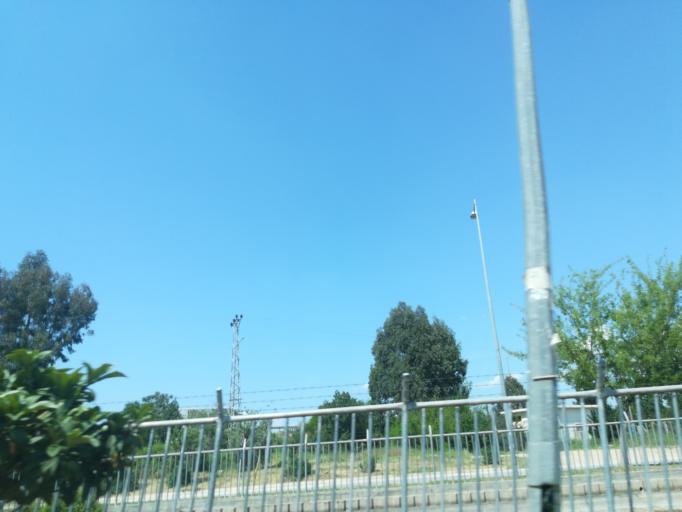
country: TR
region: Adana
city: Adana
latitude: 37.0248
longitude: 35.3649
